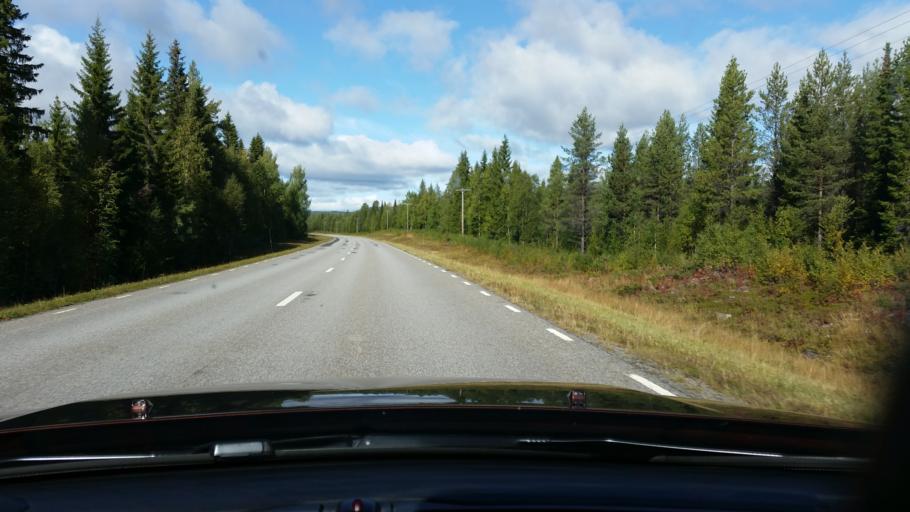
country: SE
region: Jaemtland
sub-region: Stroemsunds Kommun
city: Stroemsund
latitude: 64.2916
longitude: 15.3411
